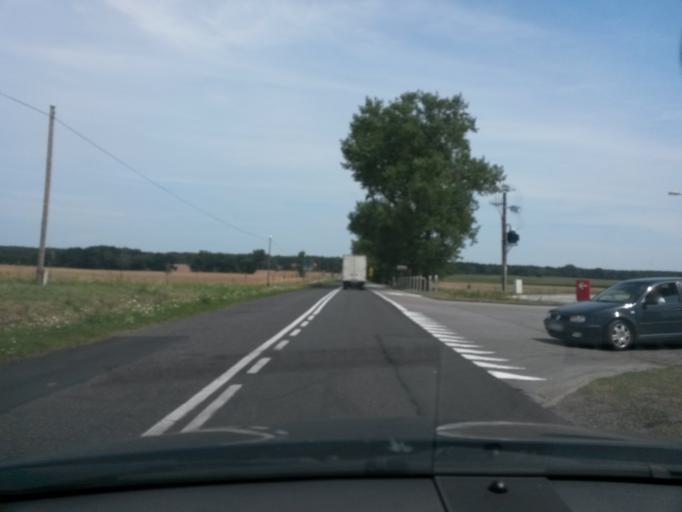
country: PL
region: Lower Silesian Voivodeship
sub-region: Powiat gorowski
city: Wasosz
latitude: 51.5713
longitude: 16.7073
